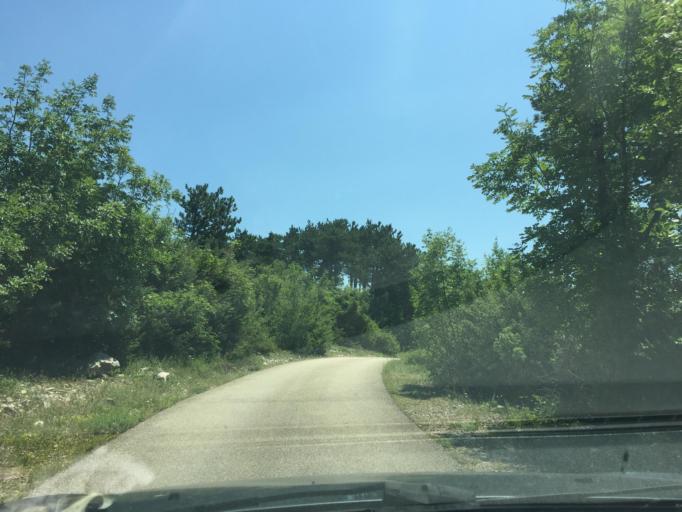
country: HR
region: Primorsko-Goranska
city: Punat
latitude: 45.0257
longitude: 14.6736
